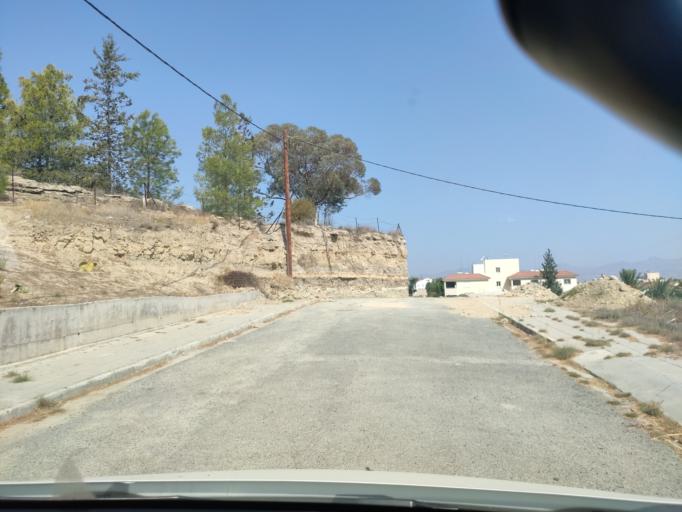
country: CY
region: Lefkosia
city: Geri
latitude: 35.1136
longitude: 33.4195
